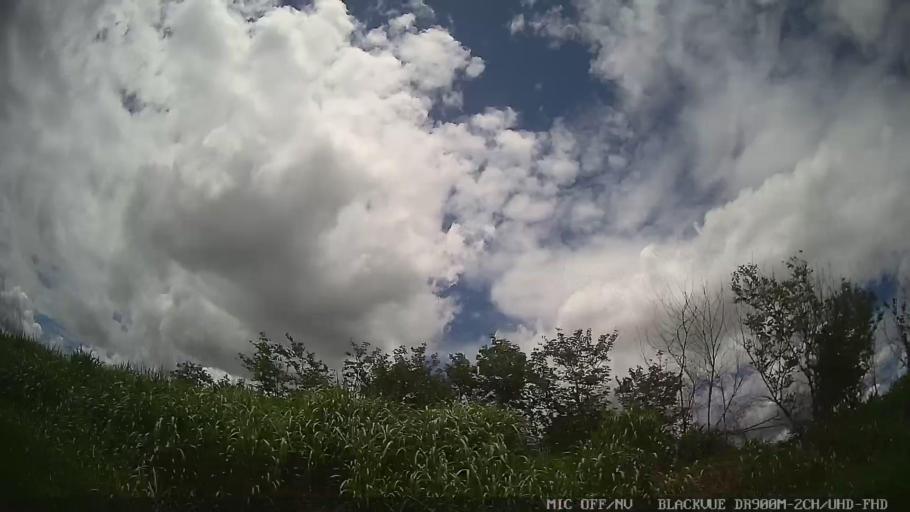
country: BR
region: Sao Paulo
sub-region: Jaguariuna
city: Jaguariuna
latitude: -22.7162
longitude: -46.9469
